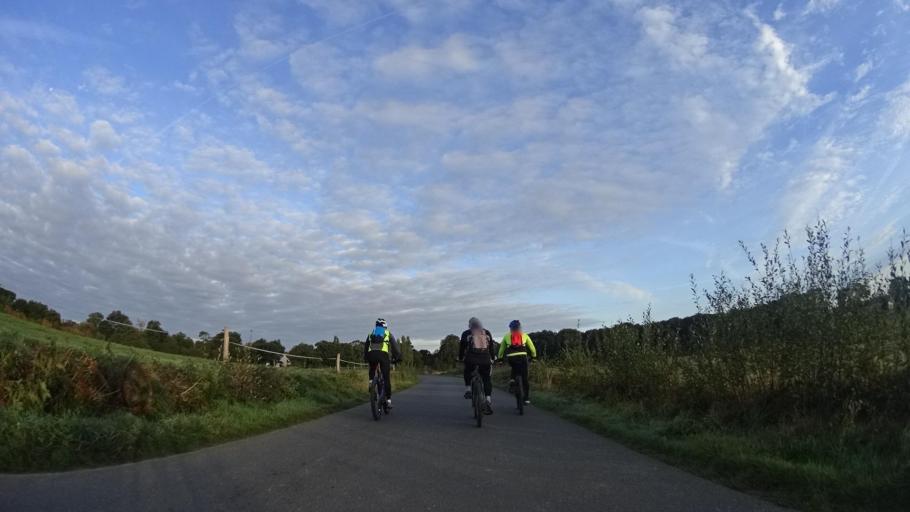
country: FR
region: Brittany
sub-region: Departement des Cotes-d'Armor
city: Evran
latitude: 48.3684
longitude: -1.9587
